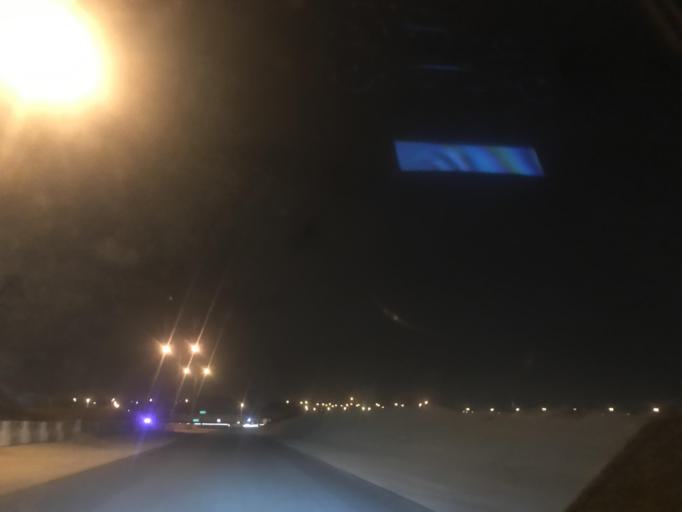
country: SA
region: Ar Riyad
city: Riyadh
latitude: 24.7590
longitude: 46.5895
